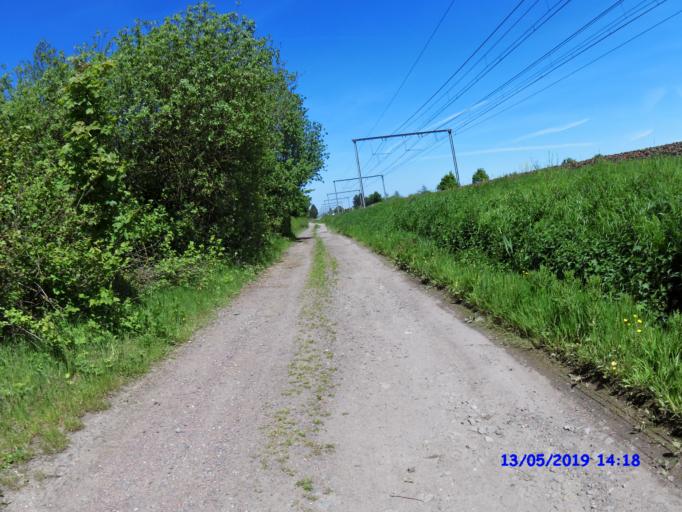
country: BE
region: Flanders
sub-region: Provincie Oost-Vlaanderen
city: Deinze
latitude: 50.9572
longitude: 3.5045
